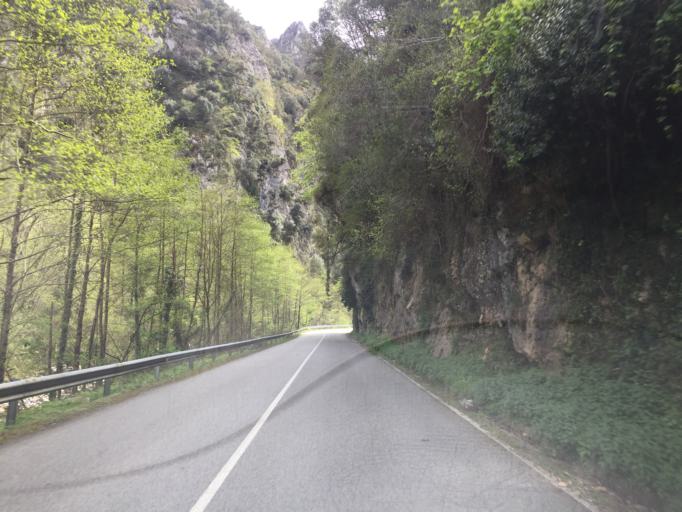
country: ES
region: Asturias
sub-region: Province of Asturias
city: Proaza
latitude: 43.2365
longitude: -6.0312
